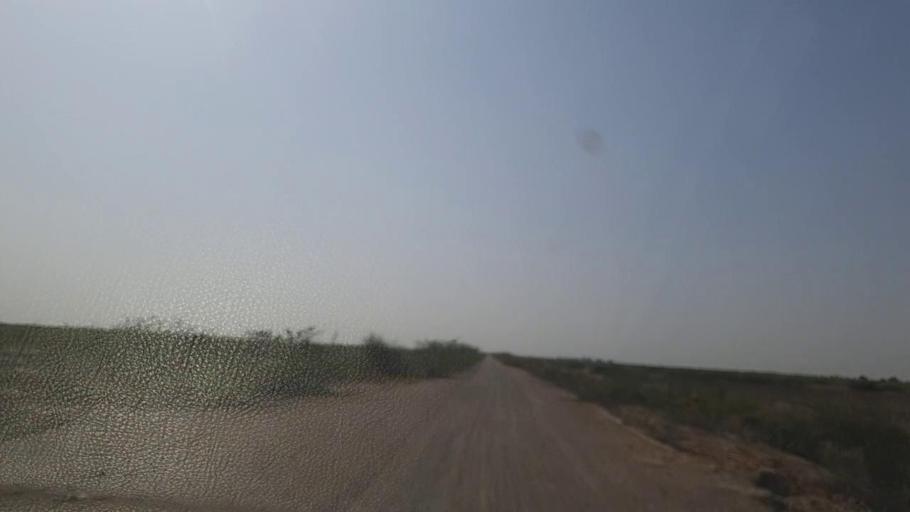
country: PK
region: Sindh
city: Naukot
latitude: 24.5925
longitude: 69.3001
